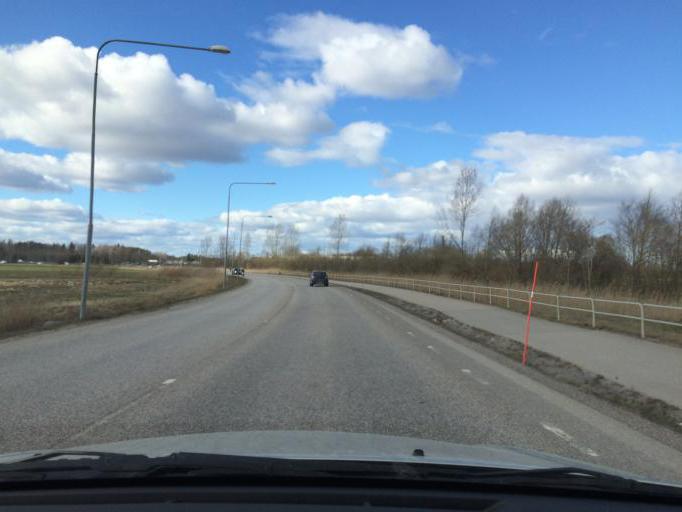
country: SE
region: Soedermanland
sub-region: Eskilstuna Kommun
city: Torshalla
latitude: 59.3919
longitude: 16.4521
